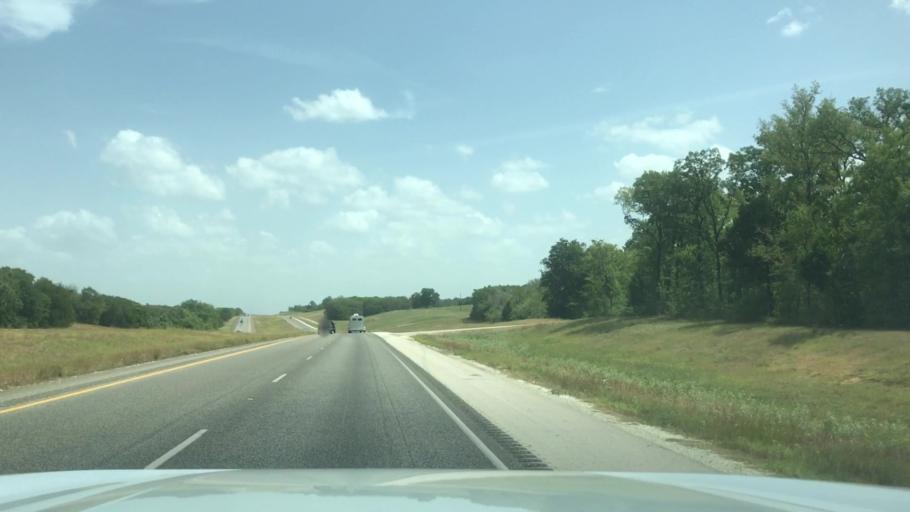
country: US
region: Texas
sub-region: Robertson County
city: Calvert
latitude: 30.9360
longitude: -96.6388
